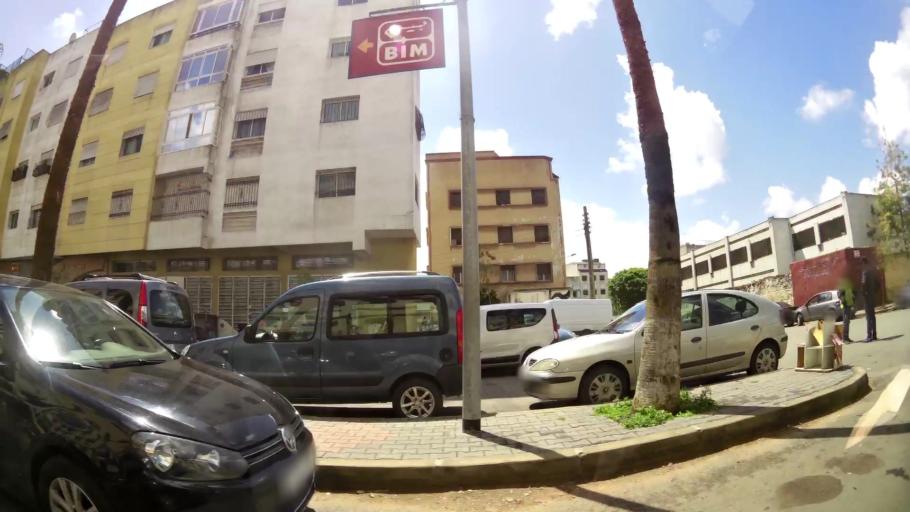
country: MA
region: Grand Casablanca
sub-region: Casablanca
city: Casablanca
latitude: 33.5599
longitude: -7.5988
